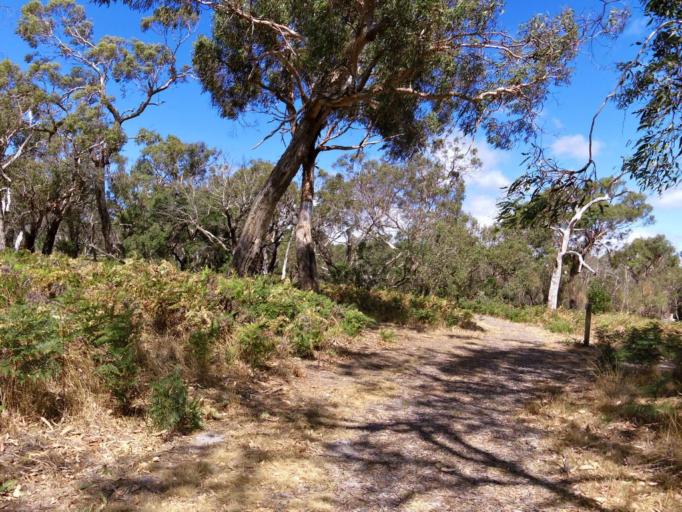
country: AU
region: Victoria
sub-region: Mornington Peninsula
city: Mount Martha
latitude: -38.2638
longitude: 145.0448
